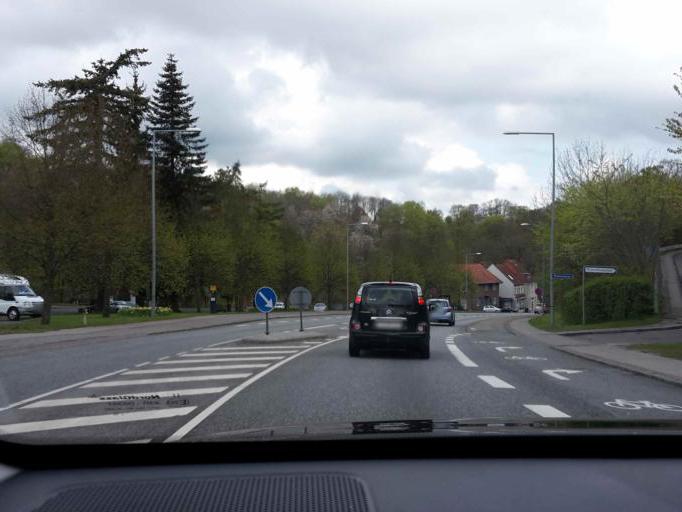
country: DK
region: South Denmark
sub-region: Vejle Kommune
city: Vejle
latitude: 55.6975
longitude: 9.5379
